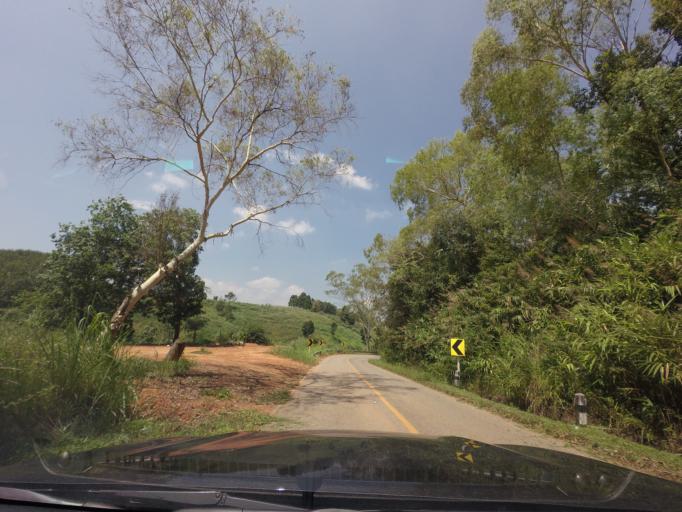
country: TH
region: Loei
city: Na Haeo
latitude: 17.5975
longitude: 100.9028
